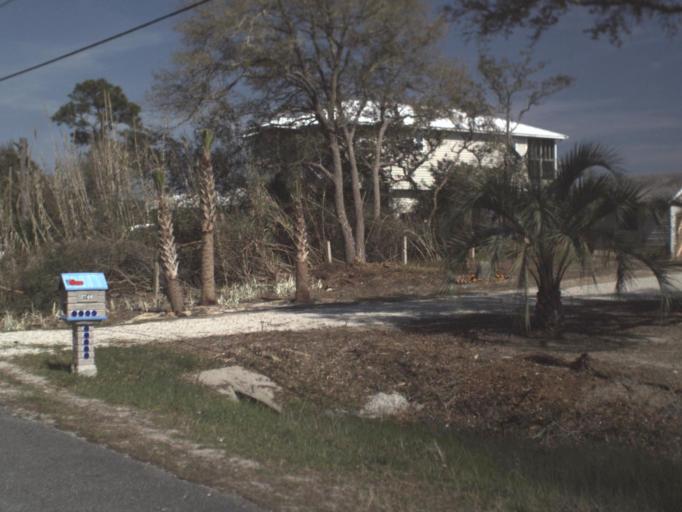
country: US
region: Florida
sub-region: Franklin County
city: Carrabelle
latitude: 29.7951
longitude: -84.7486
